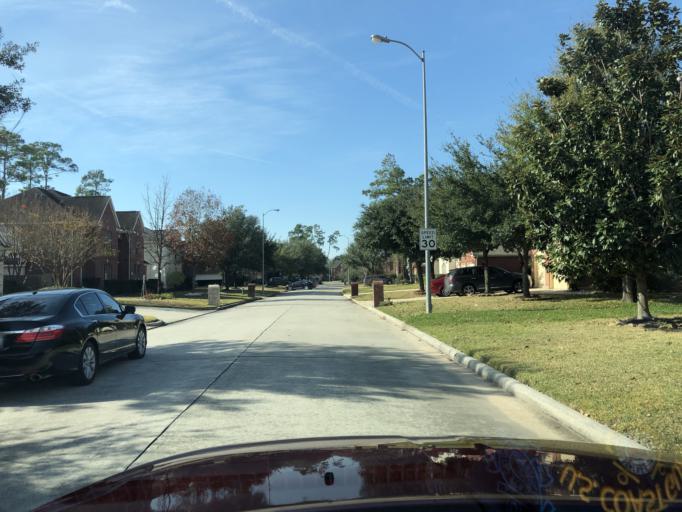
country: US
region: Texas
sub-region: Harris County
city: Tomball
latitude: 30.0272
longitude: -95.5580
